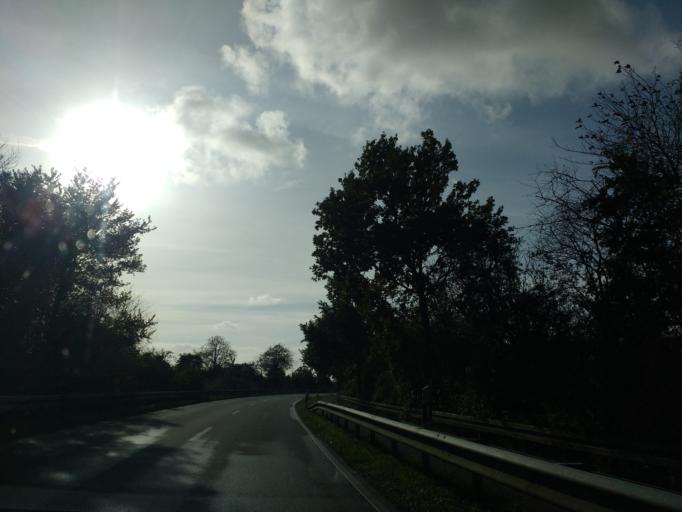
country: DE
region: Schleswig-Holstein
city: Altenkrempe
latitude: 54.1251
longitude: 10.8224
